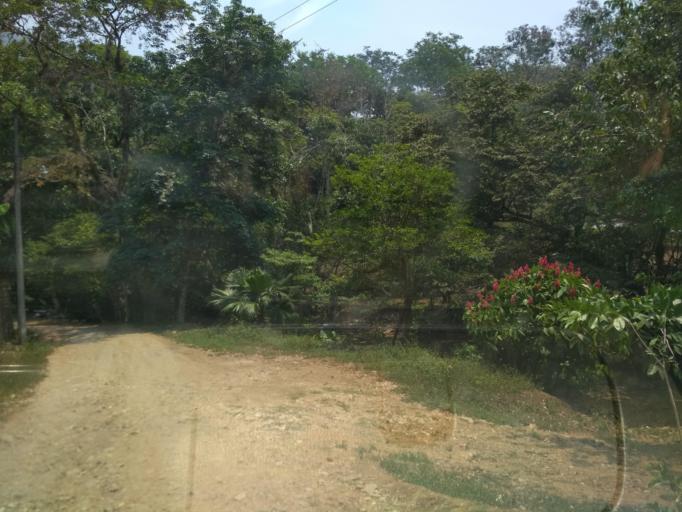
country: MX
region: Veracruz
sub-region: Tezonapa
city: Laguna Chica (Pueblo Nuevo)
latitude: 18.5680
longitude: -96.7304
